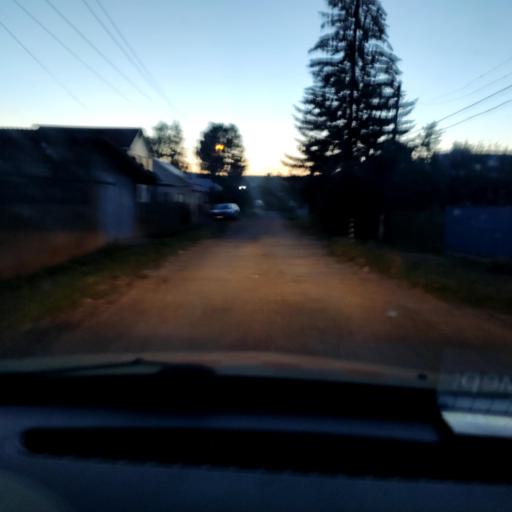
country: RU
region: Bashkortostan
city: Iglino
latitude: 54.8348
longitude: 56.4117
